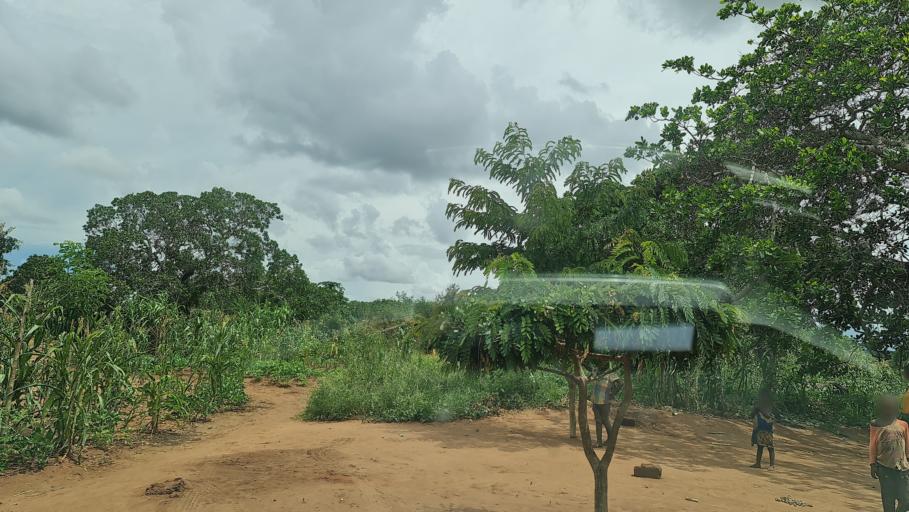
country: MZ
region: Nampula
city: Nacala
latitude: -14.7834
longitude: 39.9959
